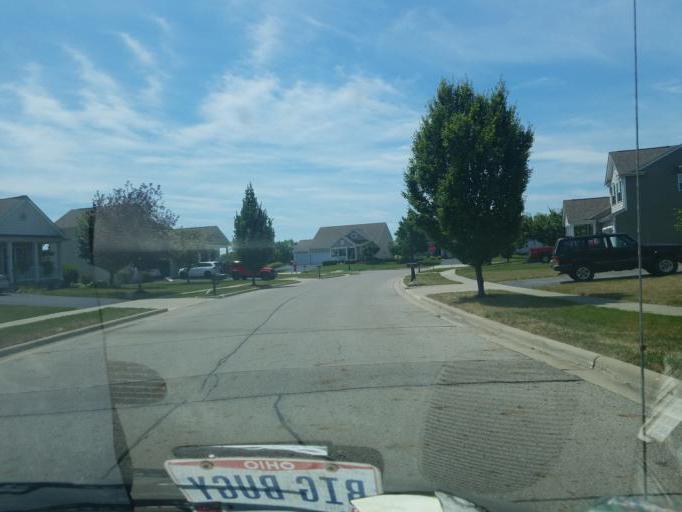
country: US
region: Ohio
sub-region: Franklin County
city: Grove City
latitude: 39.8674
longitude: -83.0982
